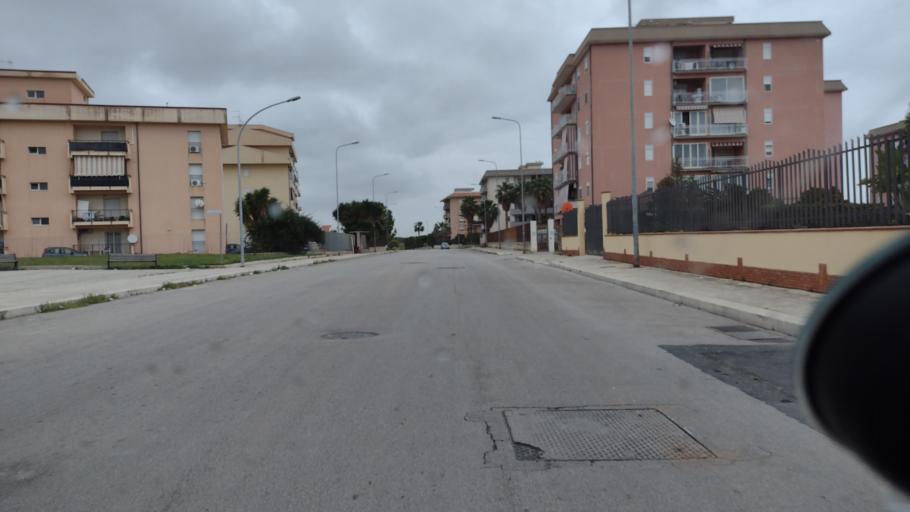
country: IT
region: Sicily
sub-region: Provincia di Siracusa
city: Avola
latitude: 36.9161
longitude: 15.1397
